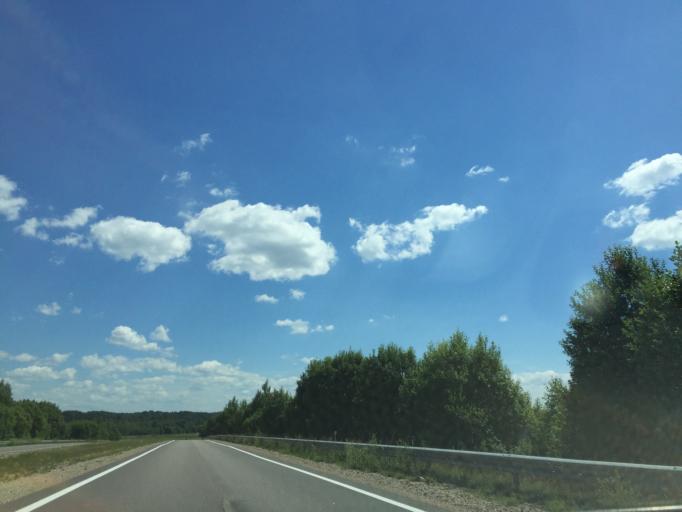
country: LV
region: Rezekne
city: Rezekne
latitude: 56.4812
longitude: 27.2902
